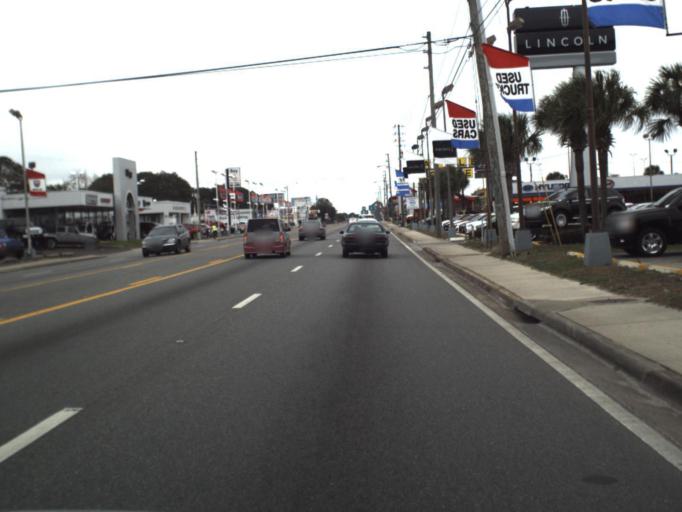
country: US
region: Florida
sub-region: Bay County
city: Panama City
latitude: 30.1751
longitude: -85.6686
